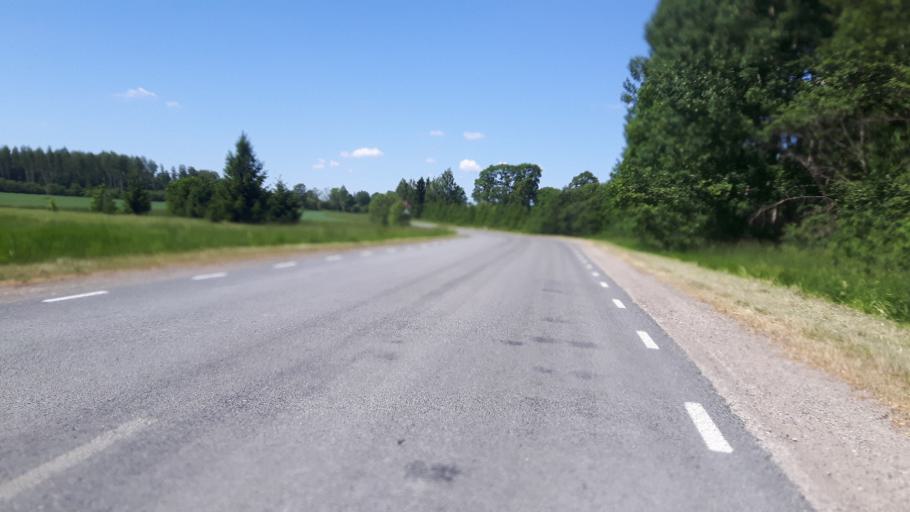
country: EE
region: Paernumaa
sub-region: Tootsi vald
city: Tootsi
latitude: 58.4938
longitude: 24.8926
